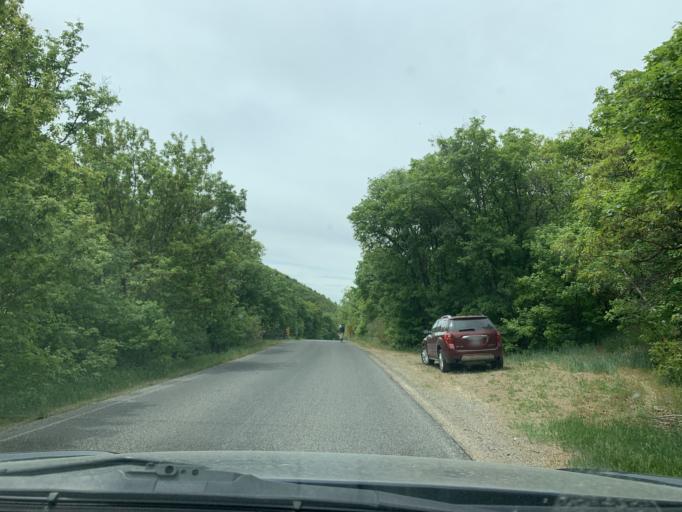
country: US
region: Utah
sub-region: Utah County
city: Mapleton
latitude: 40.1683
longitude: -111.4809
